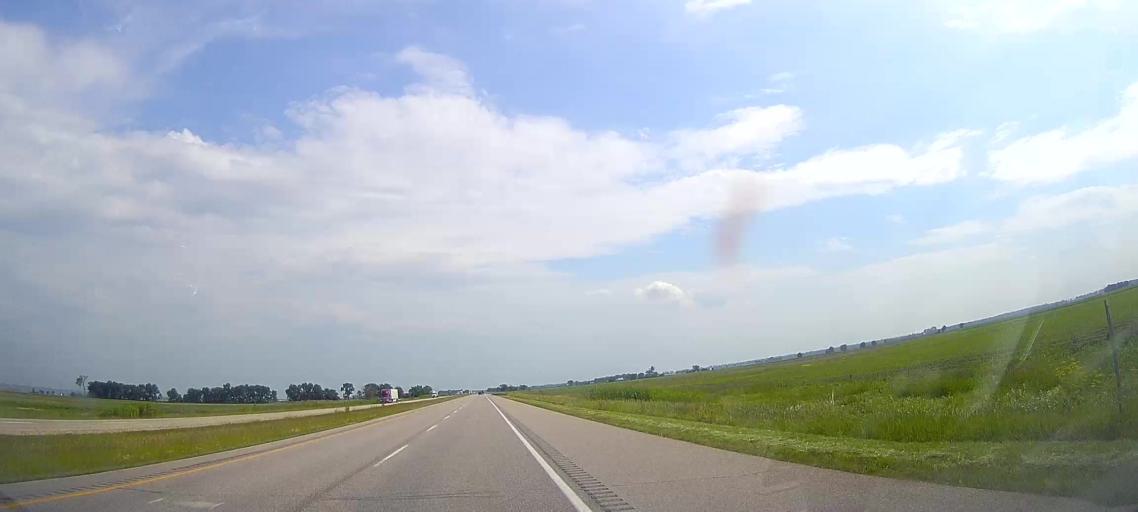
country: US
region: Iowa
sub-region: Monona County
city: Onawa
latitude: 41.9065
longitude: -96.1043
